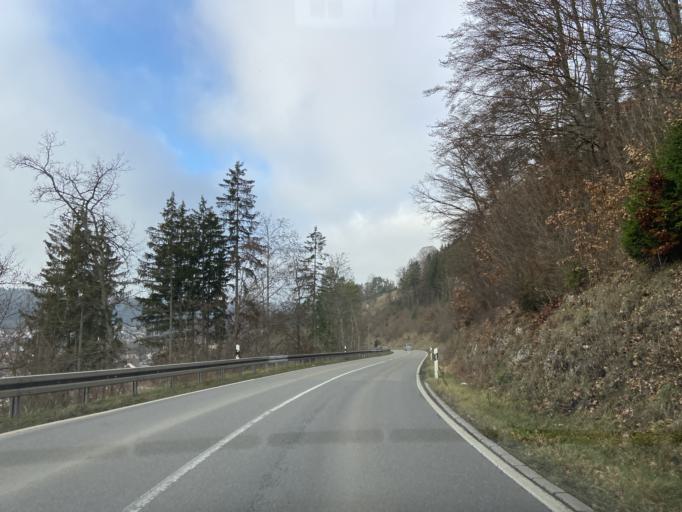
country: DE
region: Baden-Wuerttemberg
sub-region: Tuebingen Region
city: Neufra
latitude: 48.2439
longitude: 9.1913
